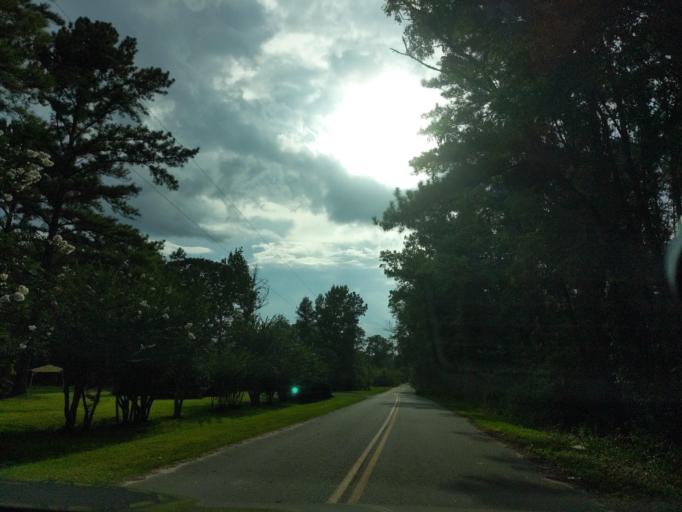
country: US
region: Florida
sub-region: Jefferson County
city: Monticello
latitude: 30.4782
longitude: -83.8942
